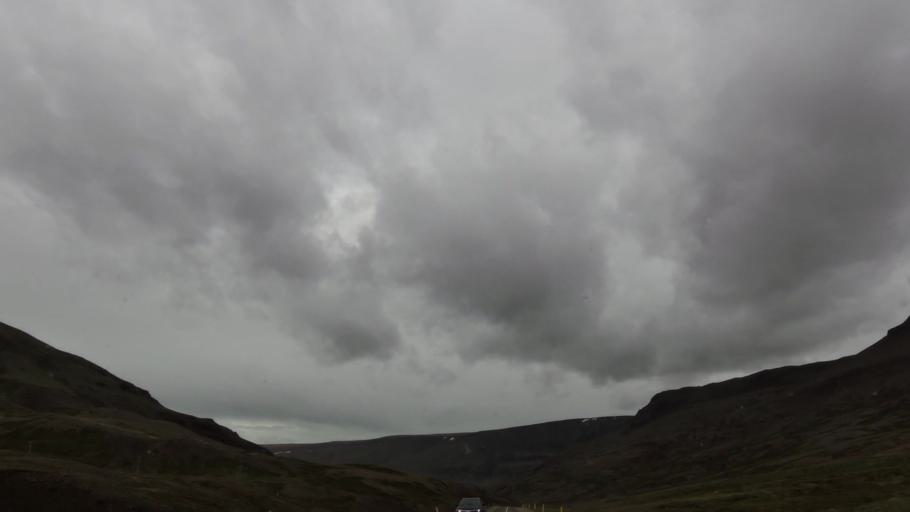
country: IS
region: West
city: Borgarnes
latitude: 65.3301
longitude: -21.7453
